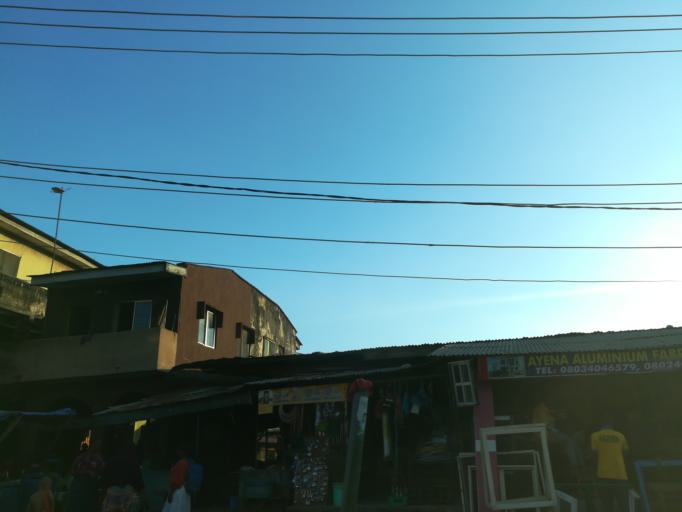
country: NG
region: Lagos
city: Ikorodu
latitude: 6.6149
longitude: 3.5103
